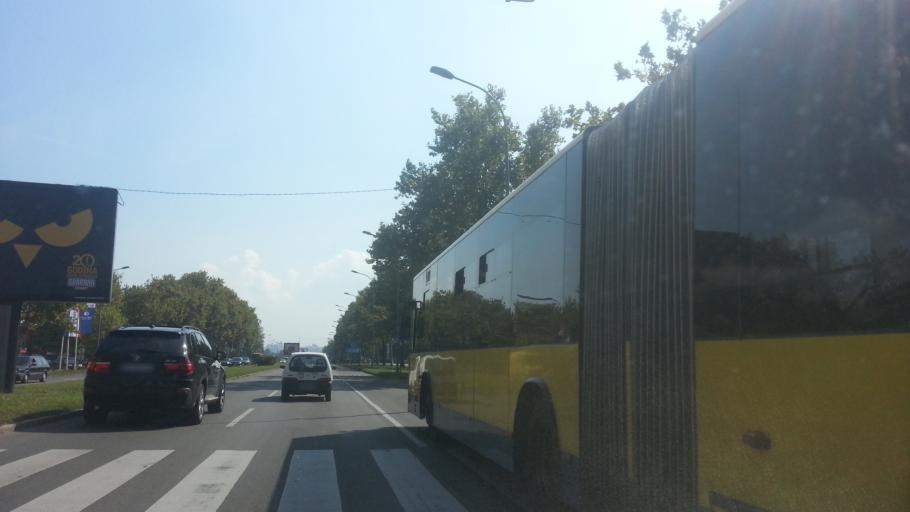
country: RS
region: Central Serbia
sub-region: Belgrade
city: Novi Beograd
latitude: 44.8212
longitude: 20.4198
